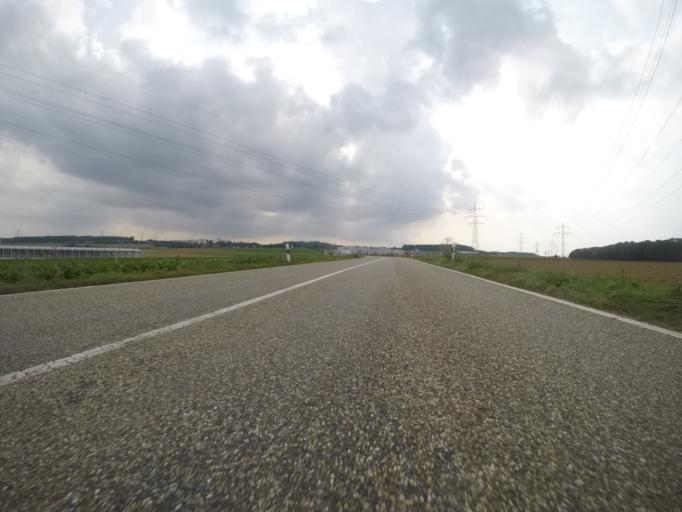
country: DE
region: Baden-Wuerttemberg
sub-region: Regierungsbezirk Stuttgart
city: Oberriexingen
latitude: 48.8961
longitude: 9.0137
